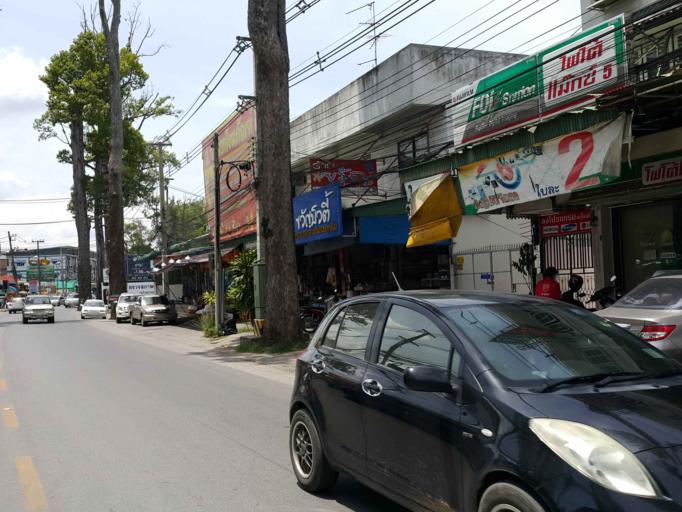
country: TH
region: Chiang Mai
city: Chiang Mai
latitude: 18.7658
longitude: 99.0056
